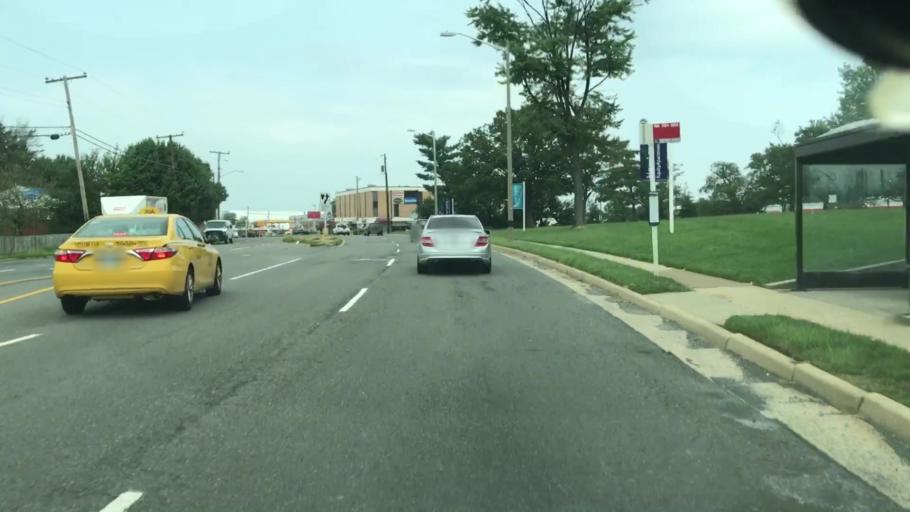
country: US
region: Virginia
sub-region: Fairfax County
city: Baileys Crossroads
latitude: 38.8448
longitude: -77.1231
